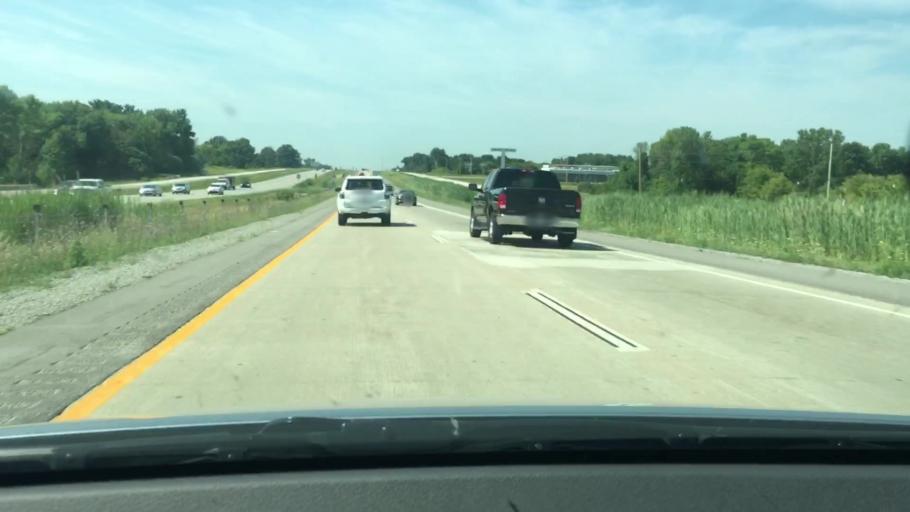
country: US
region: Wisconsin
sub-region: Brown County
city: De Pere
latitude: 44.4138
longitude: -88.1358
